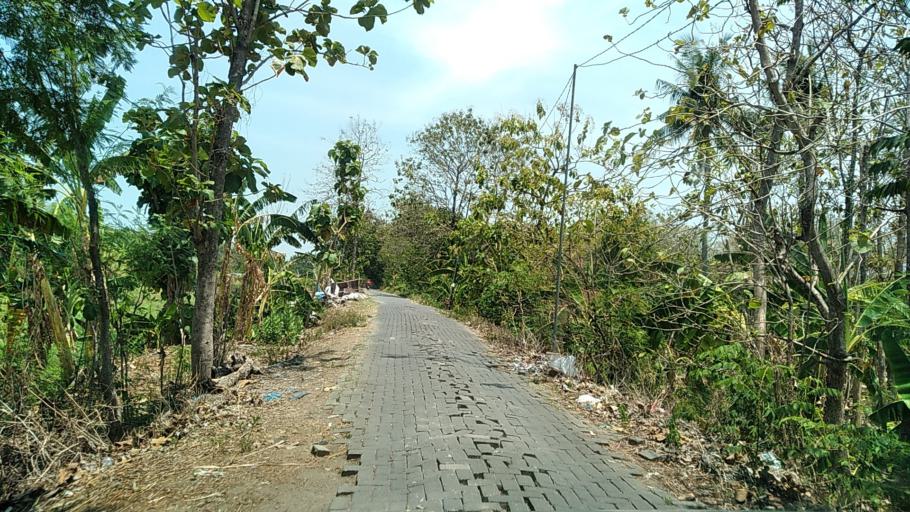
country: ID
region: Central Java
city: Mranggen
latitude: -6.9657
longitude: 110.4974
